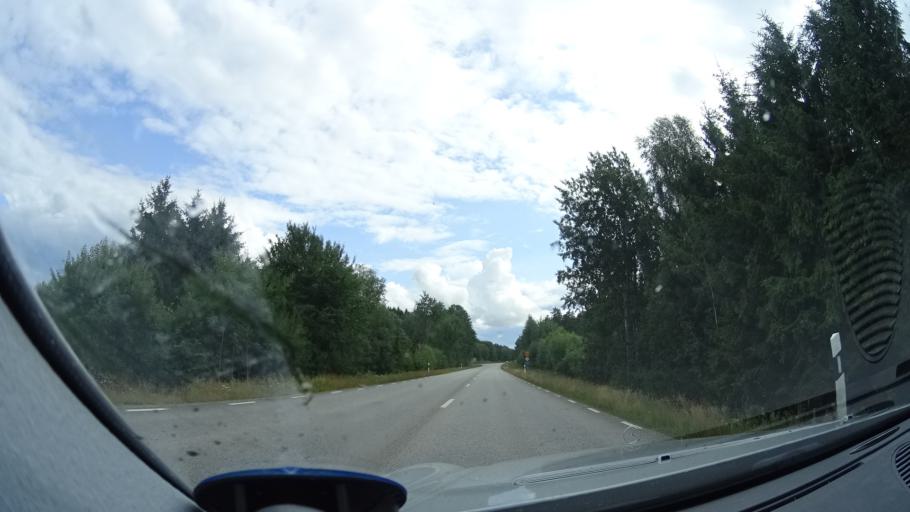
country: SE
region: Blekinge
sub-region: Karlshamns Kommun
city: Svangsta
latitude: 56.2364
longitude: 14.8266
